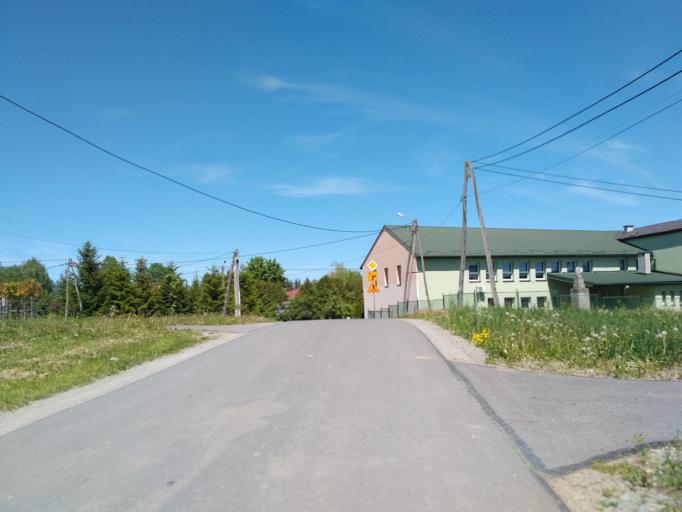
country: PL
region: Subcarpathian Voivodeship
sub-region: Powiat sanocki
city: Bukowsko
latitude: 49.5077
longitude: 22.0300
